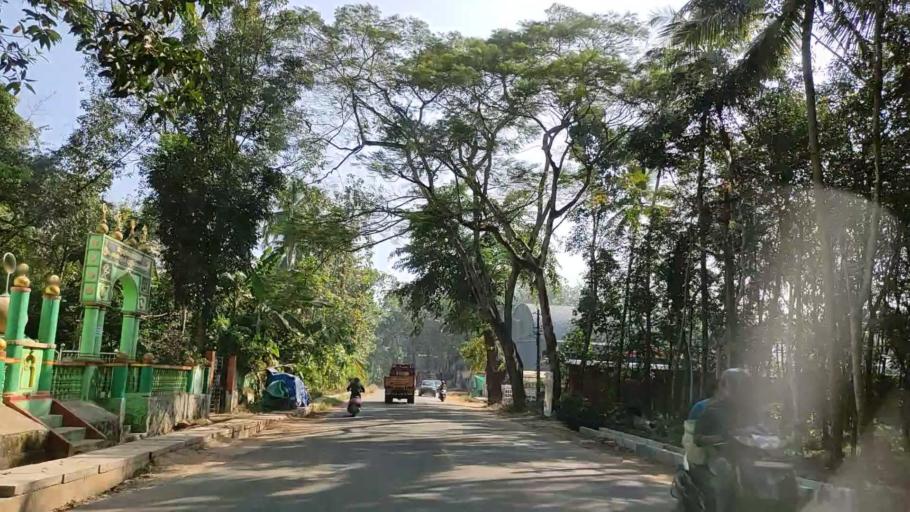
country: IN
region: Kerala
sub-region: Kollam
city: Punalur
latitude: 8.9037
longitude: 76.8710
